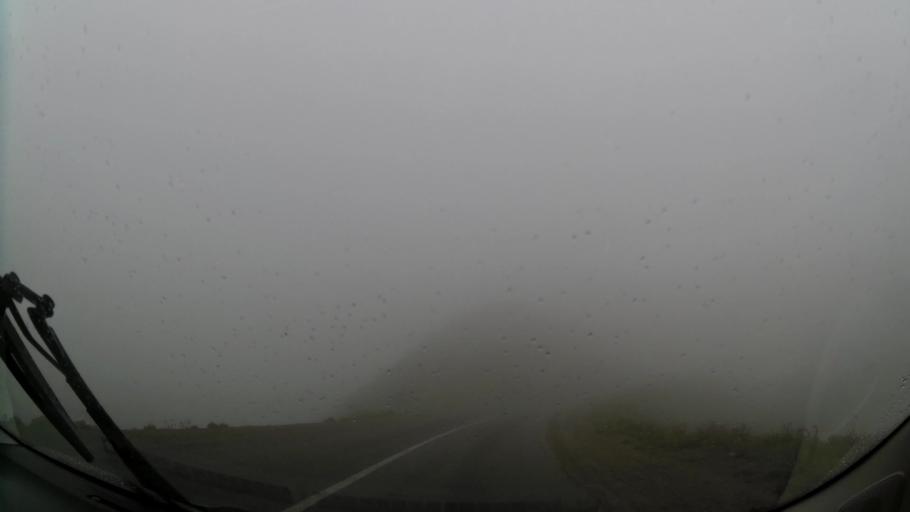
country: MA
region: Oriental
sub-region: Nador
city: Boudinar
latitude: 35.0953
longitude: -3.5463
